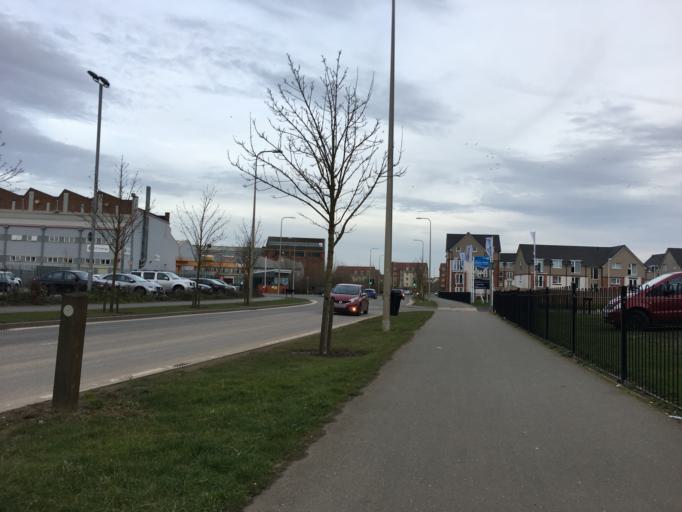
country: GB
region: England
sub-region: Warwickshire
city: Rugby
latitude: 52.3835
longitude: -1.2583
